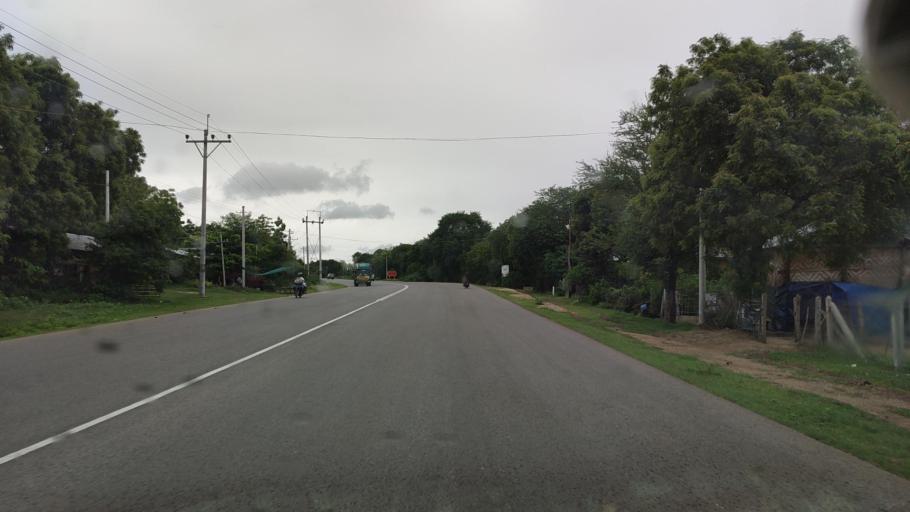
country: MM
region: Mandalay
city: Meiktila
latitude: 20.8173
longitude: 95.9062
